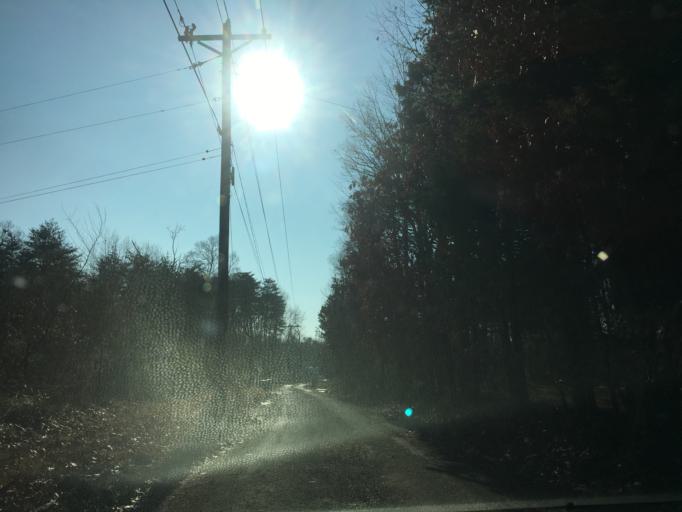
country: US
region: Virginia
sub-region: Fairfax County
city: Fairfax Station
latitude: 38.8230
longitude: -77.3670
